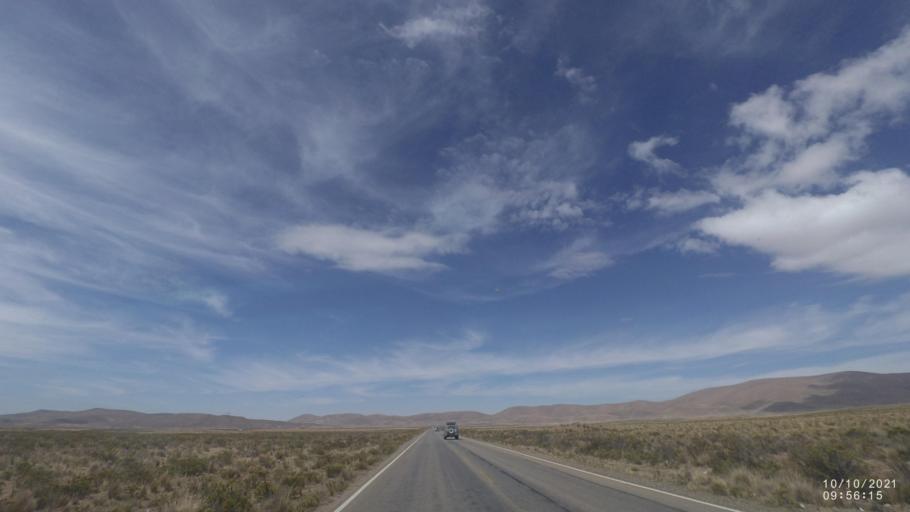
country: BO
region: La Paz
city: Colquiri
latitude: -17.3197
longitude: -67.3732
